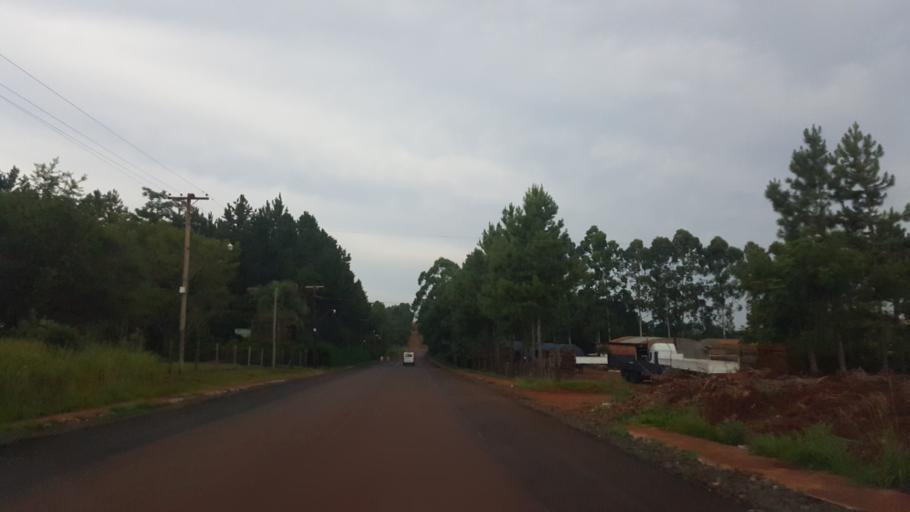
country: AR
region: Misiones
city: Puerto Leoni
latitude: -27.0039
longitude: -55.1641
